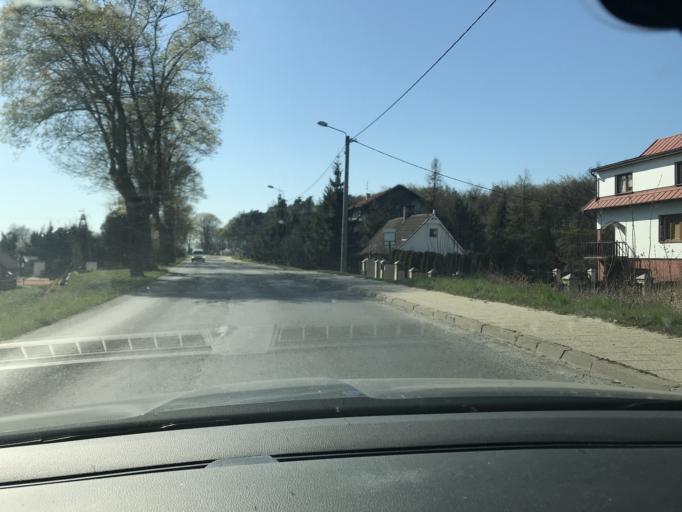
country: PL
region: Pomeranian Voivodeship
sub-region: Powiat nowodworski
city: Sztutowo
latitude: 54.3266
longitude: 19.1598
